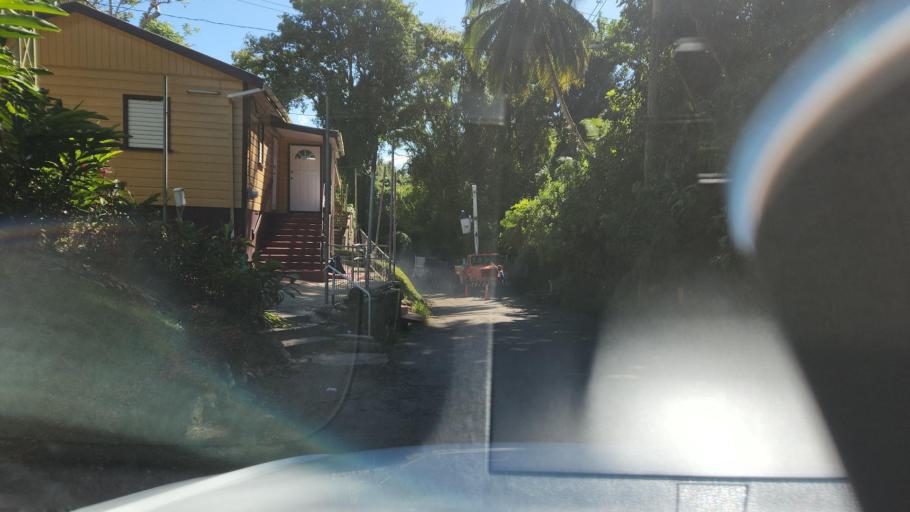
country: BB
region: Saint Thomas
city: Welchman Hall
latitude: 13.1925
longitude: -59.5955
